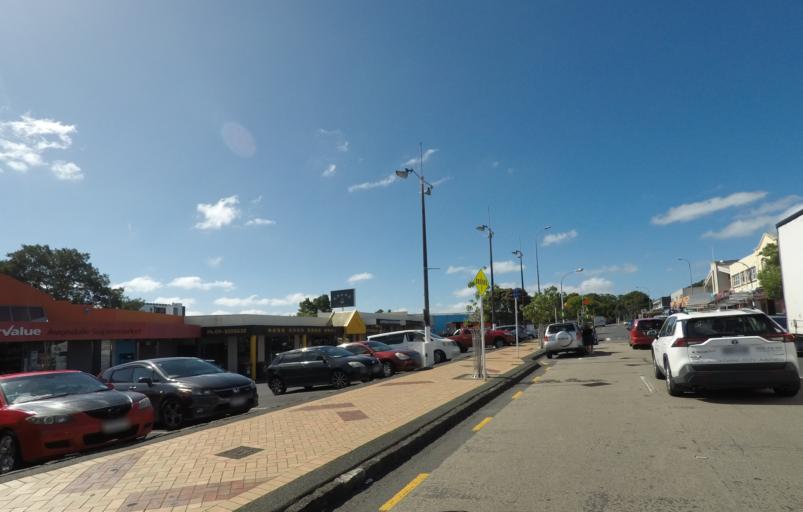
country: NZ
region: Auckland
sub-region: Auckland
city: Rosebank
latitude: -36.8981
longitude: 174.6970
